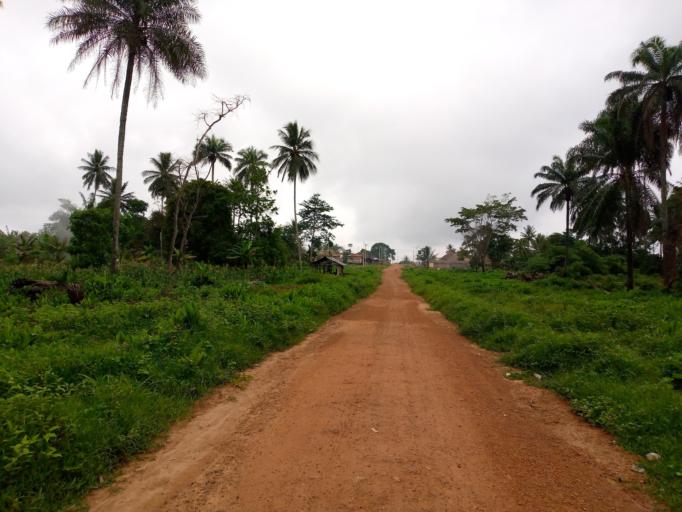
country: SL
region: Southern Province
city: Sumbuya
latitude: 7.5620
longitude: -12.0862
